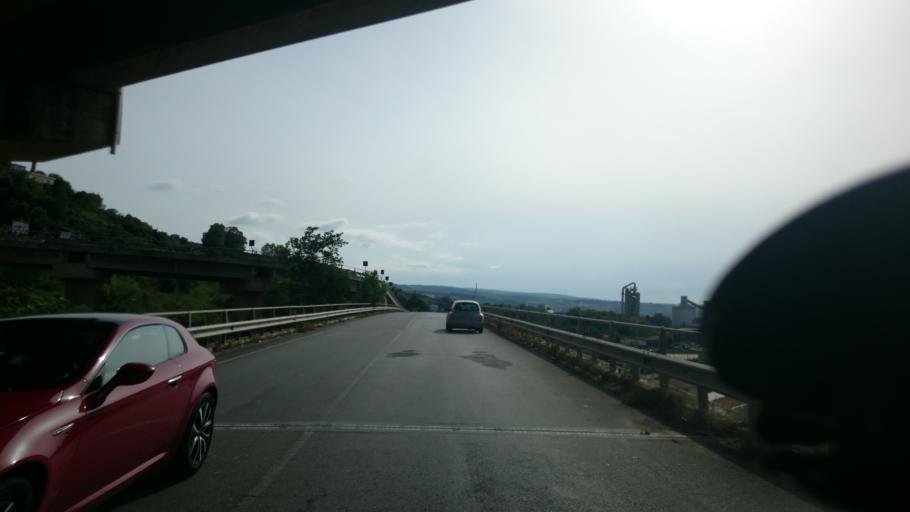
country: IT
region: Calabria
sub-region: Provincia di Vibo-Valentia
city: Sant'Onofrio
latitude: 38.7100
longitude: 16.1229
